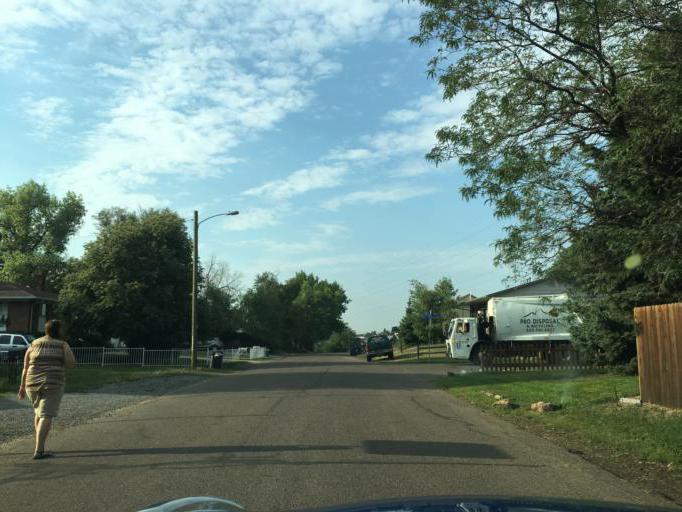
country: US
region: Colorado
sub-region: Jefferson County
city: Wheat Ridge
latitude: 39.7442
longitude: -105.1050
